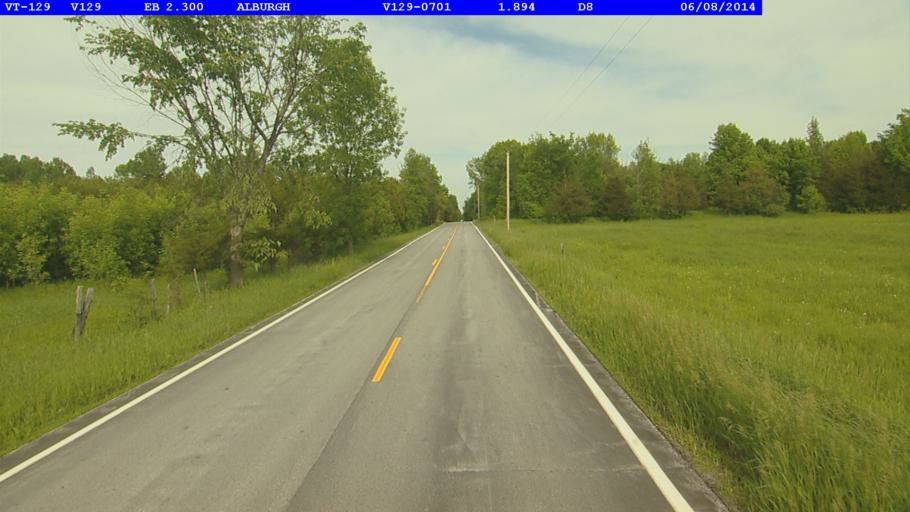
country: US
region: Vermont
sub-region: Grand Isle County
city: North Hero
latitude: 44.8874
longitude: -73.2966
